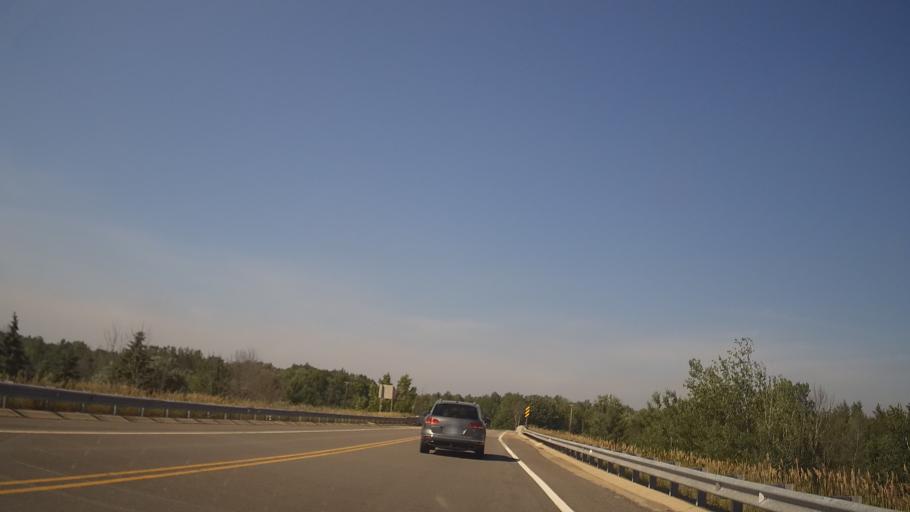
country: US
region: Michigan
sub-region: Ogemaw County
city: Skidway Lake
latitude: 44.1345
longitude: -84.1292
